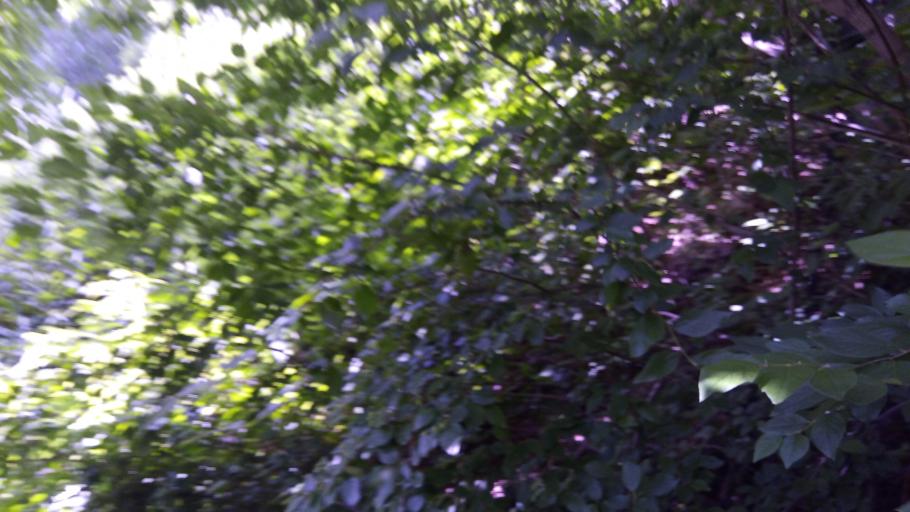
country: RU
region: Chelyabinsk
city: Chebarkul'
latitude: 55.0204
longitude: 60.3123
